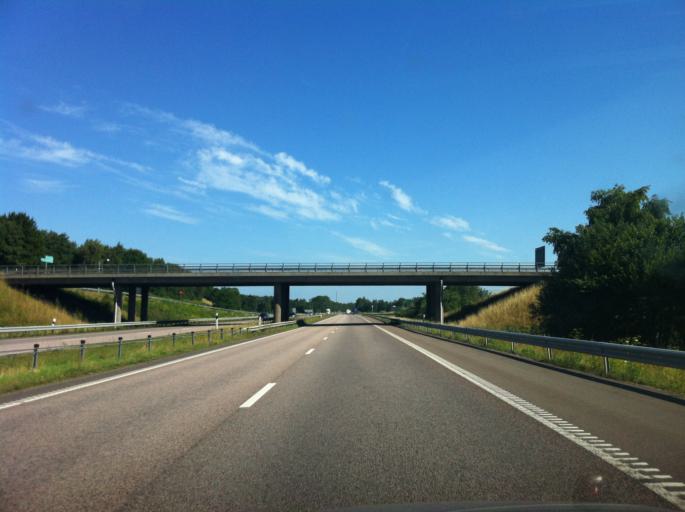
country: SE
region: Skane
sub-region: Helsingborg
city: Odakra
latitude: 56.0638
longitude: 12.7816
